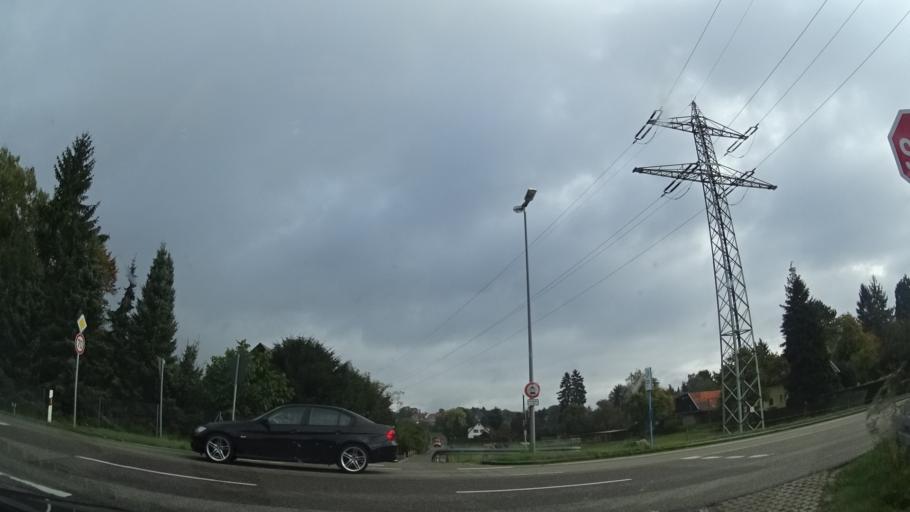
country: DE
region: Baden-Wuerttemberg
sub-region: Karlsruhe Region
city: Pforzheim
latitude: 48.9077
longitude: 8.6966
